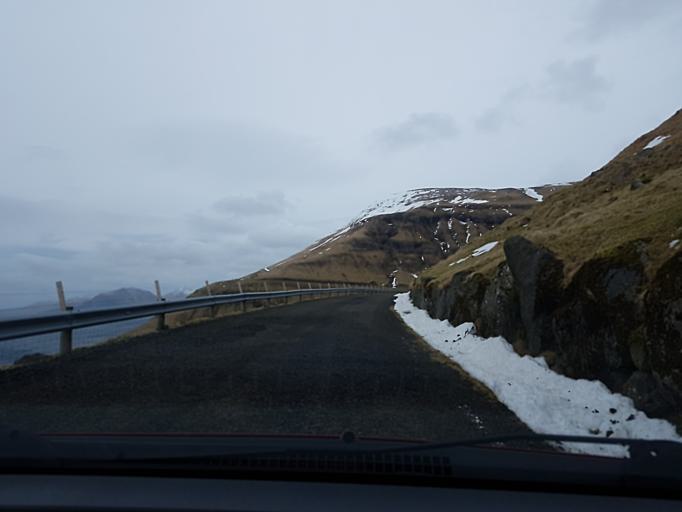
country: FO
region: Streymoy
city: Hoyvik
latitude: 61.9942
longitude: -6.8858
